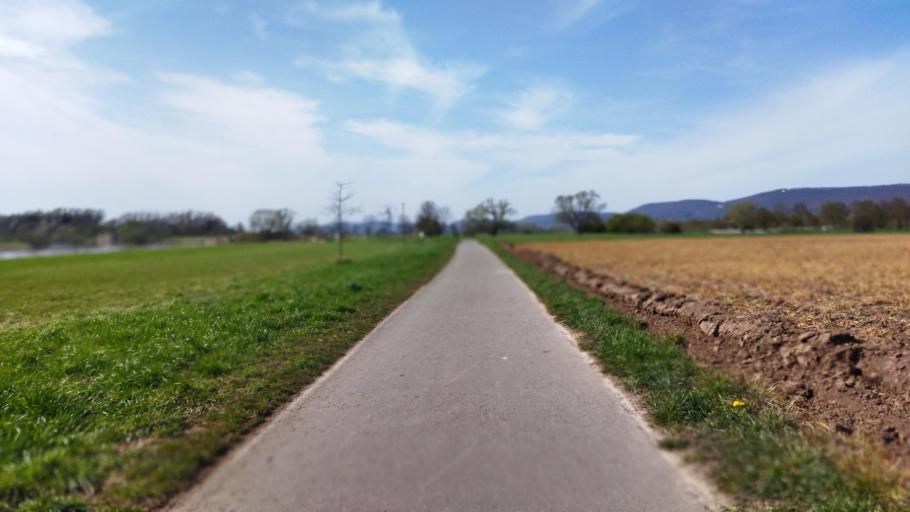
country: DE
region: Lower Saxony
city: Hessisch Oldendorf
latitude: 52.1611
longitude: 9.2411
